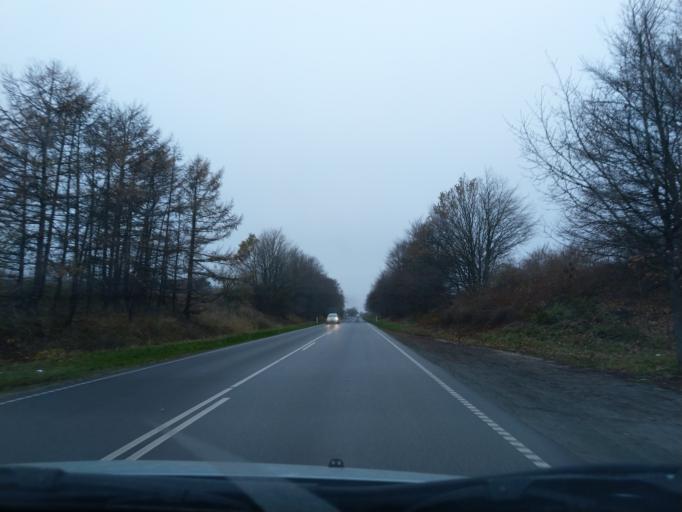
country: DK
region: Zealand
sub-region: Vordingborg Kommune
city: Praesto
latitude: 55.1150
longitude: 12.0313
